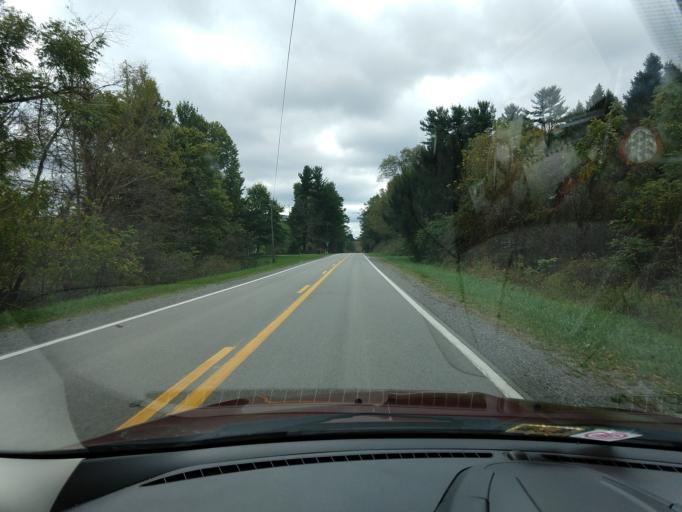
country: US
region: West Virginia
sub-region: Barbour County
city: Philippi
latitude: 39.0961
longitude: -79.9945
